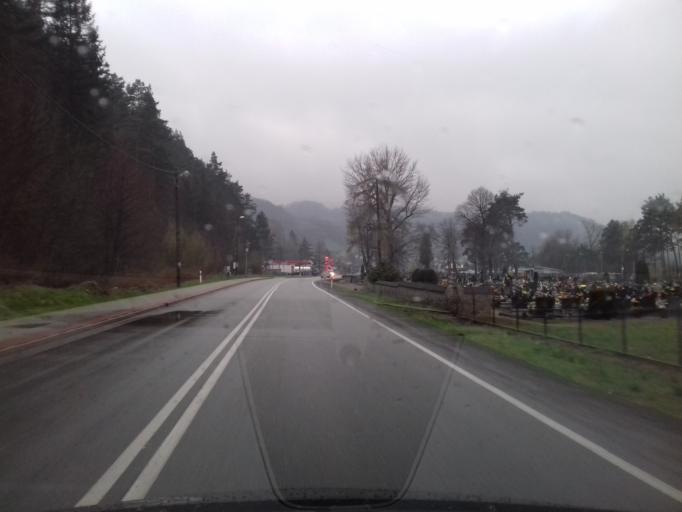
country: PL
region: Lesser Poland Voivodeship
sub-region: Powiat nowosadecki
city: Piwniczna-Zdroj
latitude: 49.4471
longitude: 20.7072
